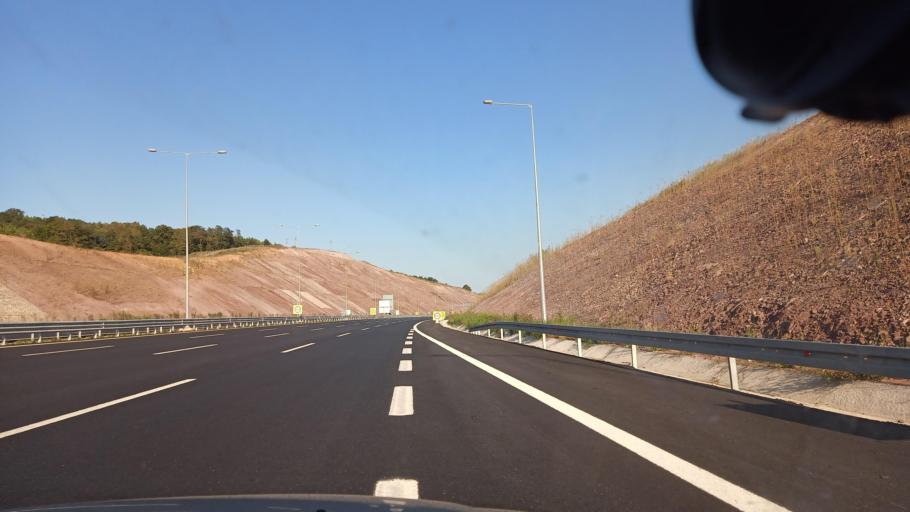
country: TR
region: Sakarya
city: Adapazari
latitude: 40.8393
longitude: 30.3733
